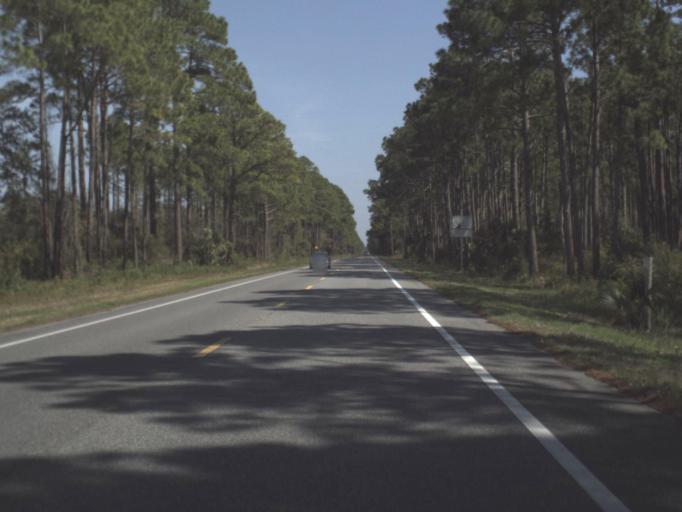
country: US
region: Florida
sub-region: Franklin County
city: Apalachicola
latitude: 29.7176
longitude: -85.0539
